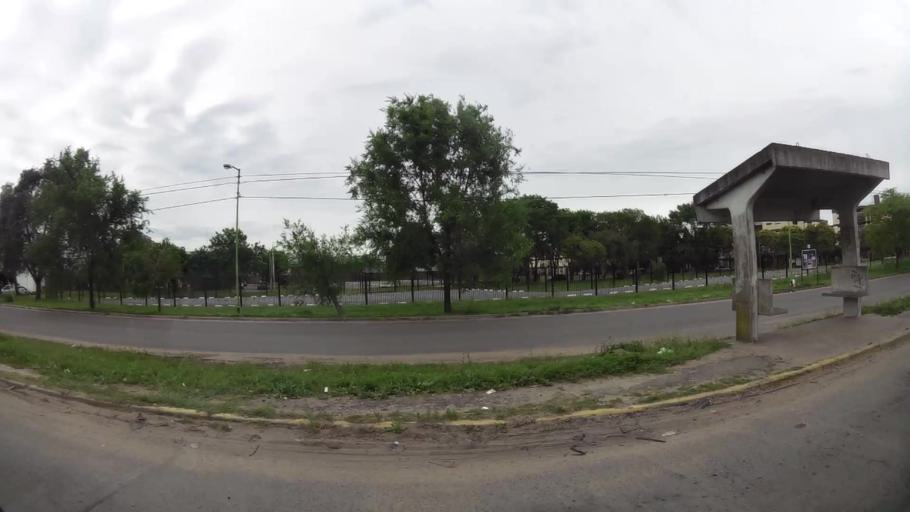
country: AR
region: Buenos Aires
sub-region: Partido de Campana
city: Campana
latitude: -34.1862
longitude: -58.9434
